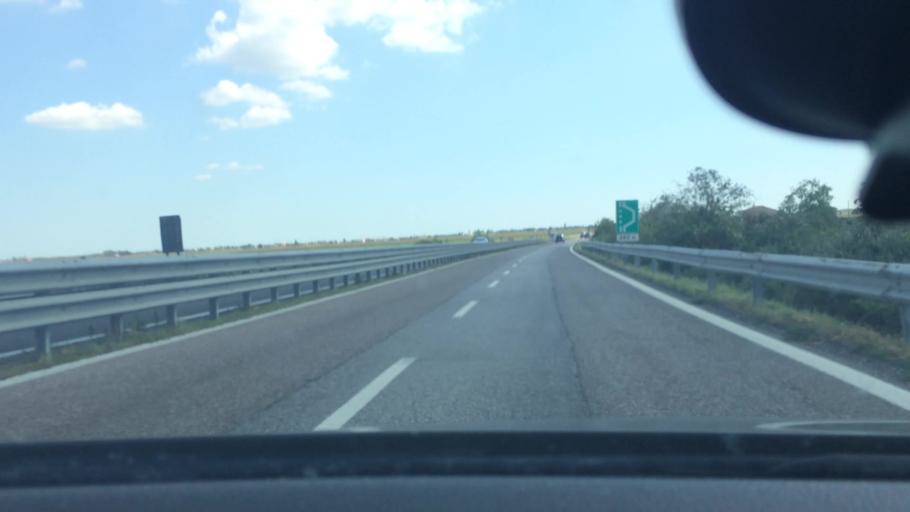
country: IT
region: Emilia-Romagna
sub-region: Provincia di Ferrara
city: Ostellato
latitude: 44.7562
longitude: 11.9656
